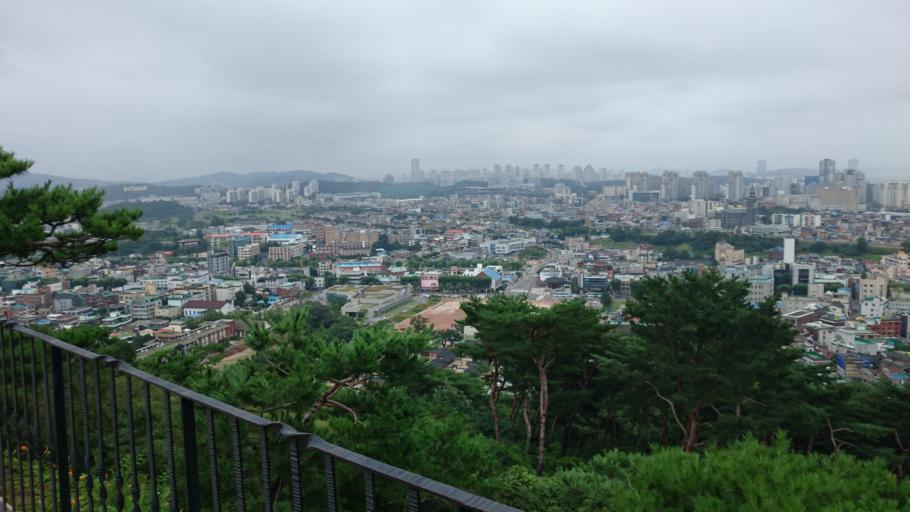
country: KR
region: Gyeonggi-do
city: Suwon-si
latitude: 37.2807
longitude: 127.0104
